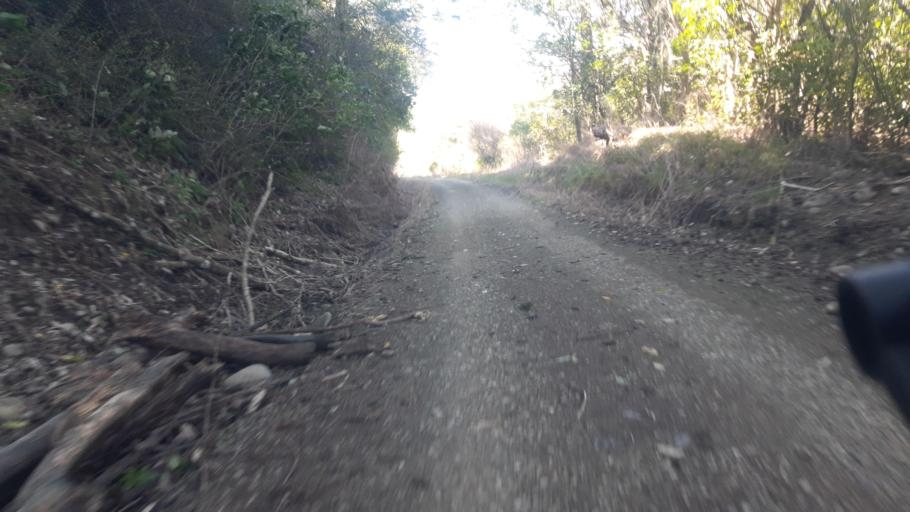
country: NZ
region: Tasman
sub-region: Tasman District
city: Wakefield
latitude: -41.4865
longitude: 172.9285
